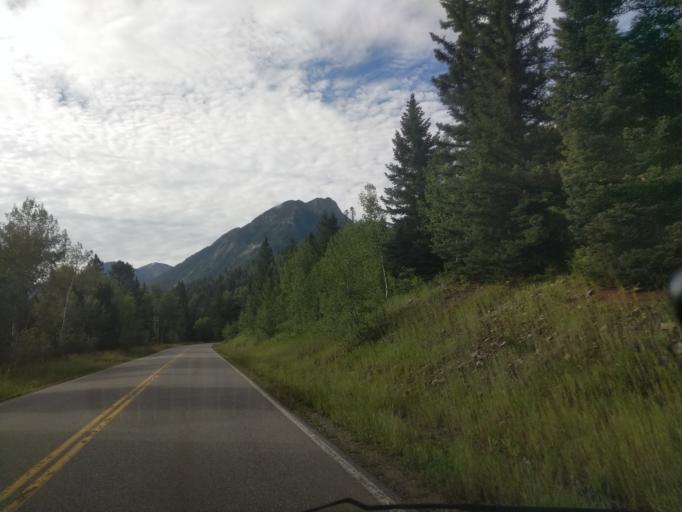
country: US
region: Colorado
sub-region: Garfield County
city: Carbondale
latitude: 39.0969
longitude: -107.2576
